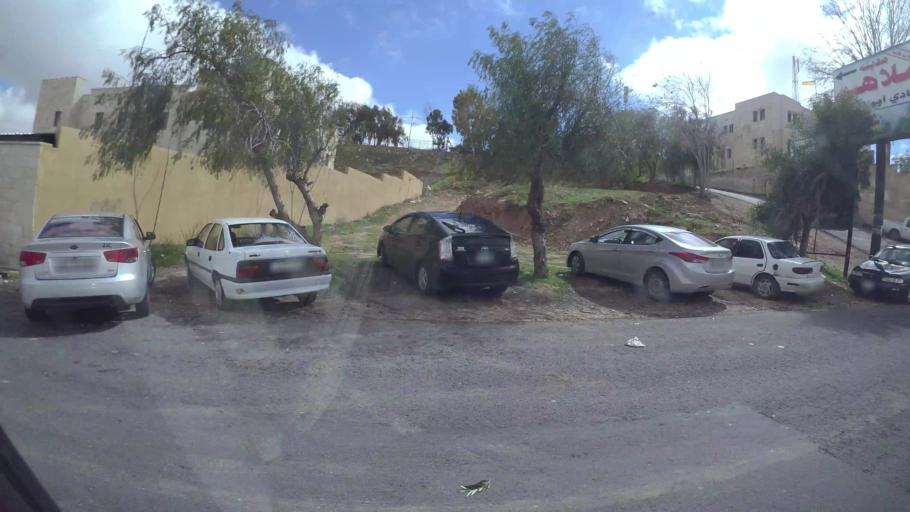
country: JO
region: Amman
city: Al Jubayhah
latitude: 32.0623
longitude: 35.8845
